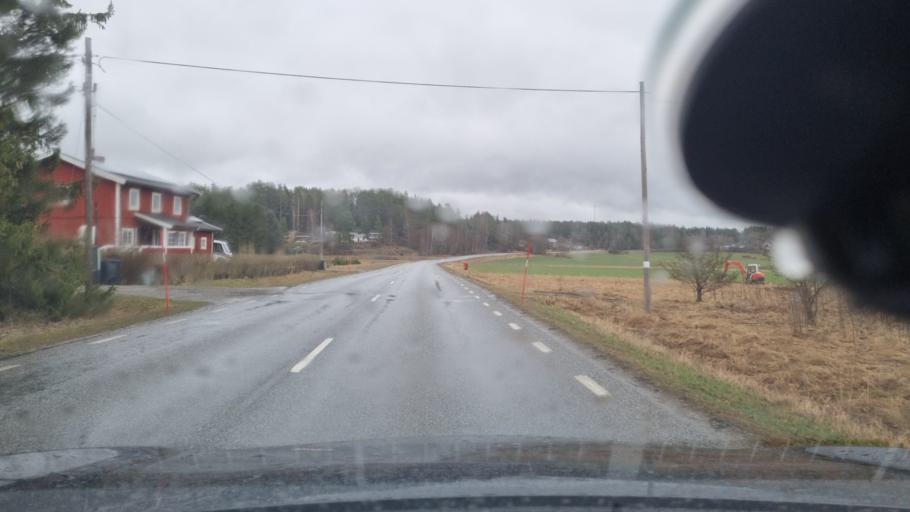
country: SE
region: Stockholm
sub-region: Sigtuna Kommun
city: Sigtuna
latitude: 59.5847
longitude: 17.6650
